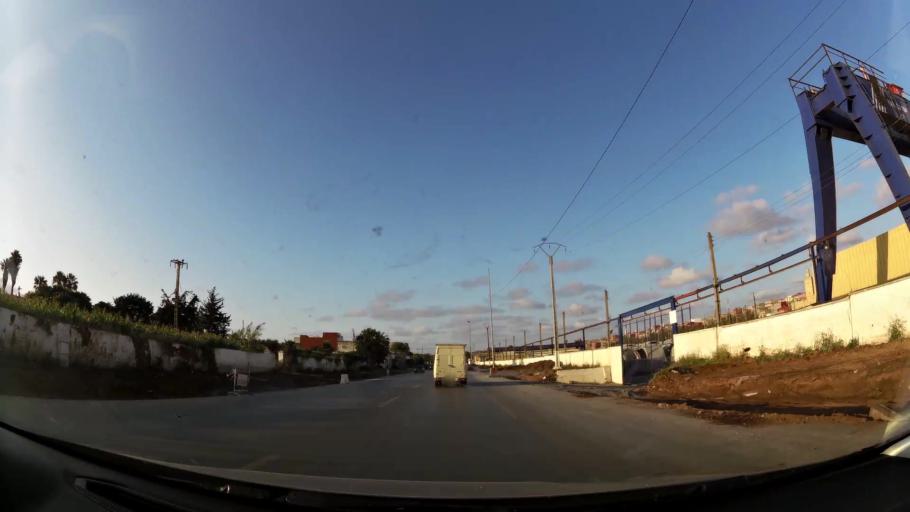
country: MA
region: Rabat-Sale-Zemmour-Zaer
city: Sale
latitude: 34.1172
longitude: -6.7440
